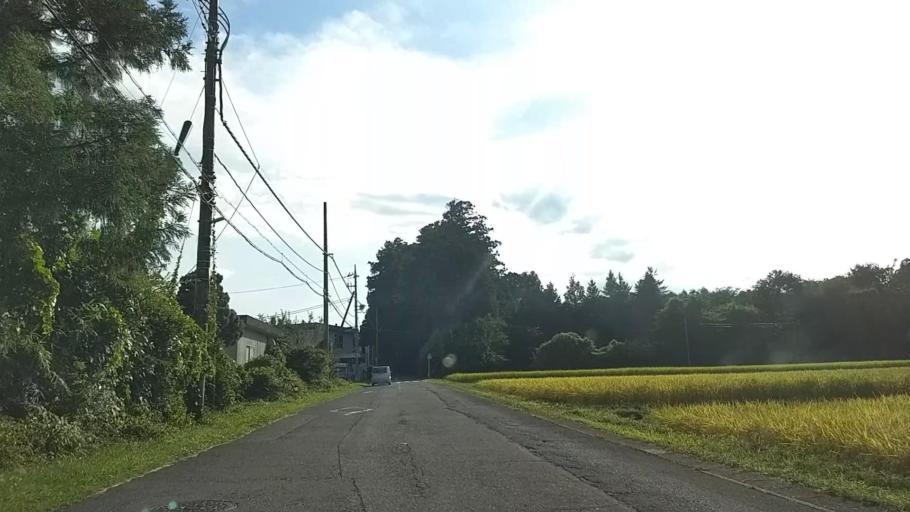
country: JP
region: Tochigi
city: Imaichi
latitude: 36.7397
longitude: 139.7025
